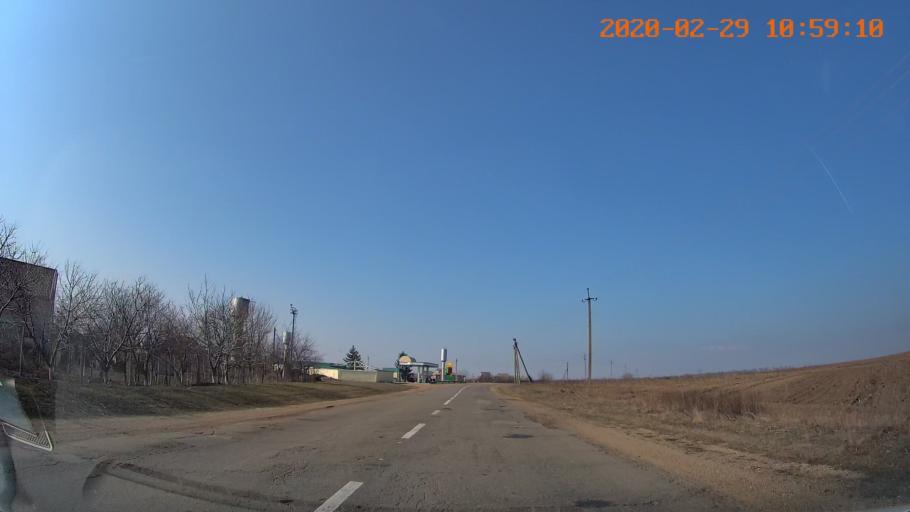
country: MD
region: Telenesti
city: Grigoriopol
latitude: 47.1645
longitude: 29.2968
